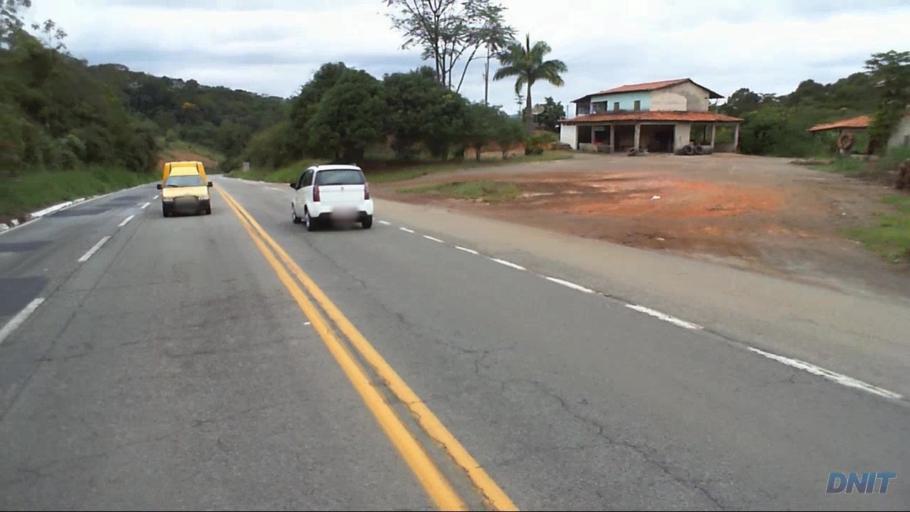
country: BR
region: Minas Gerais
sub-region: Barao De Cocais
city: Barao de Cocais
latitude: -19.7975
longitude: -43.4203
